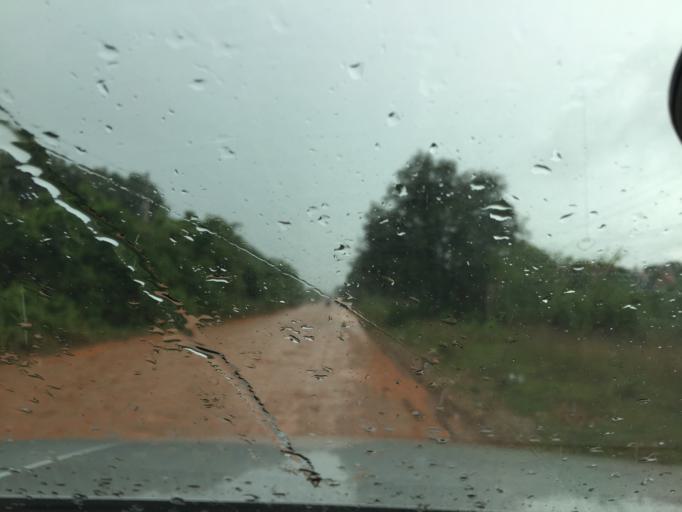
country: LA
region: Attapu
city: Attapu
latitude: 14.8299
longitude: 106.8021
